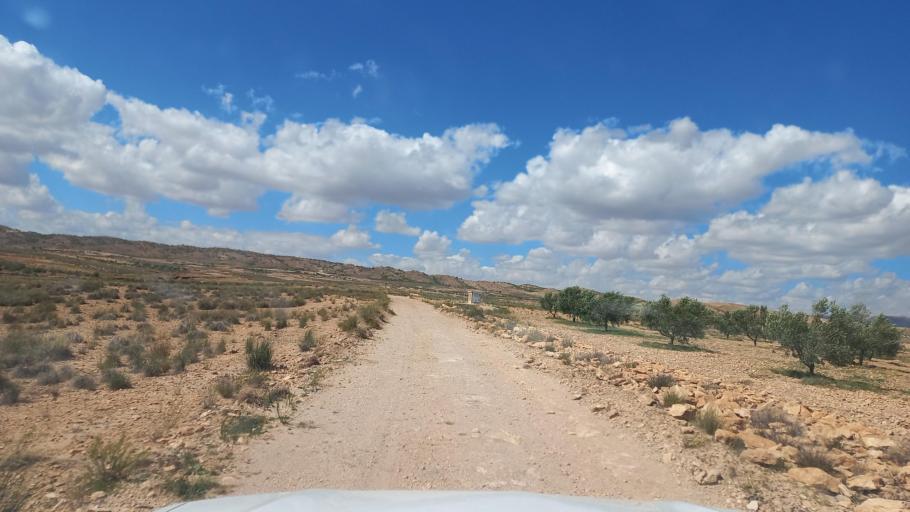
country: TN
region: Al Qasrayn
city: Sbiba
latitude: 35.3551
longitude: 9.0113
